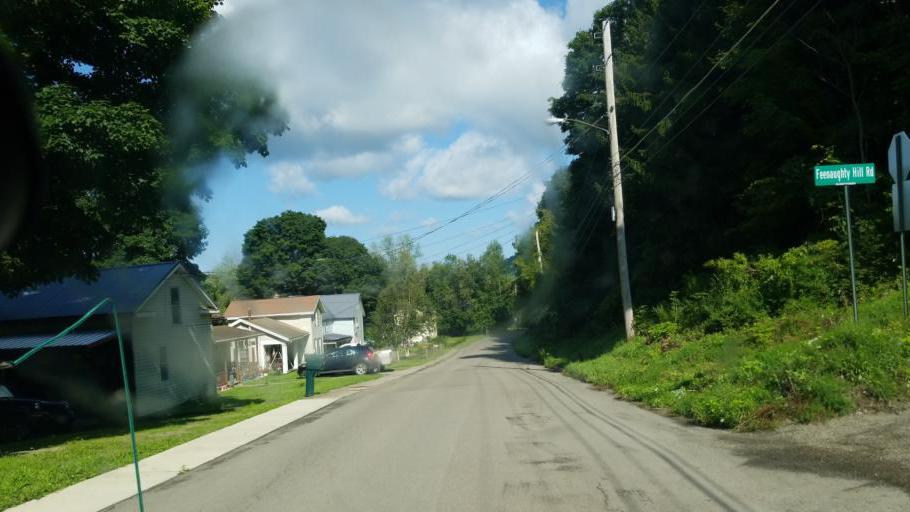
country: US
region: New York
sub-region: Steuben County
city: Canisteo
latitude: 42.2804
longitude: -77.6029
